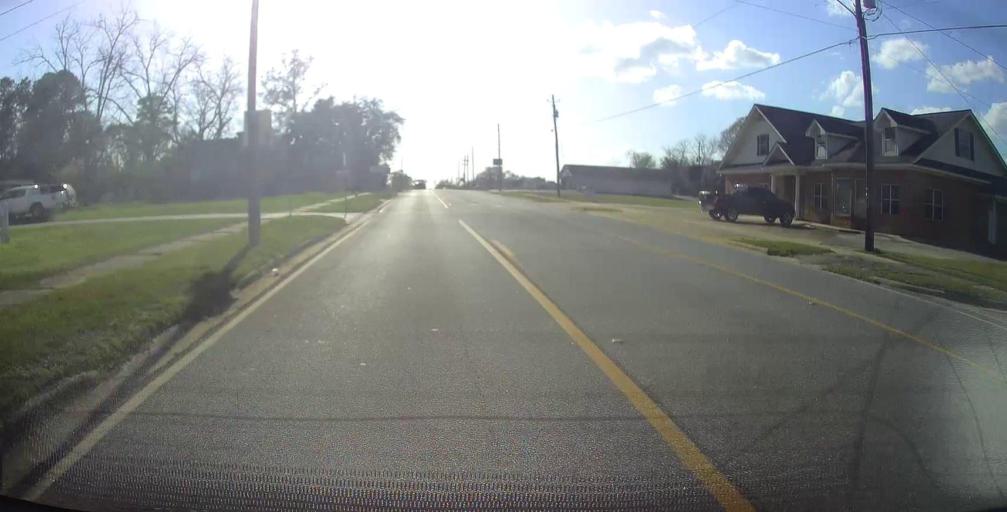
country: US
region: Georgia
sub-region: Montgomery County
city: Mount Vernon
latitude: 32.1806
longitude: -82.6674
